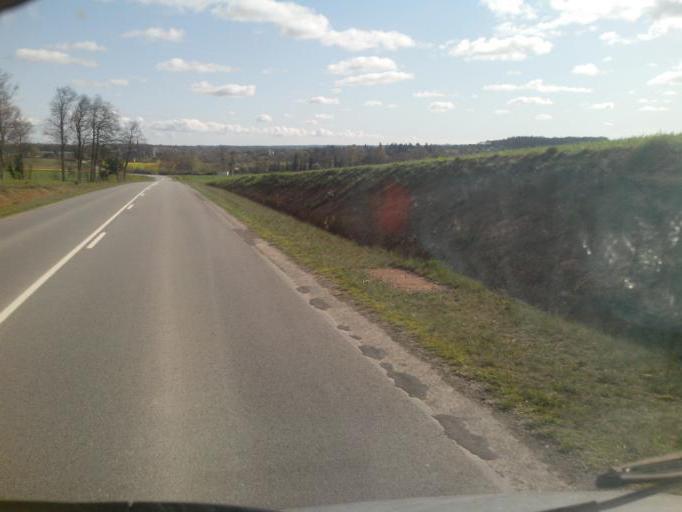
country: FR
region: Brittany
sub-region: Departement d'Ille-et-Vilaine
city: Maure-de-Bretagne
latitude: 47.9051
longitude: -1.9914
